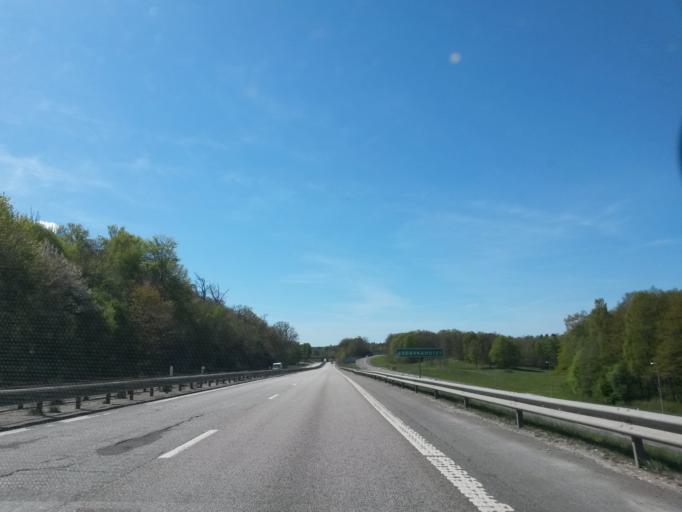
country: SE
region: Vaestra Goetaland
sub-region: Alingsas Kommun
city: Alingsas
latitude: 57.9030
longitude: 12.4989
